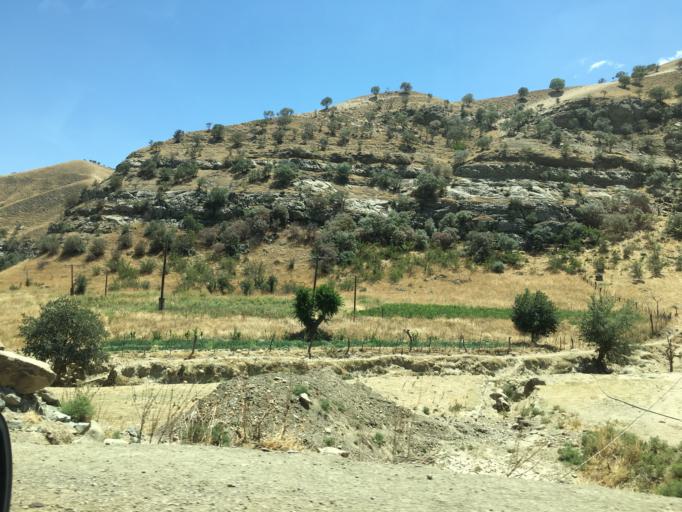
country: TM
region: Balkan
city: Magtymguly
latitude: 38.4235
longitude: 56.6498
